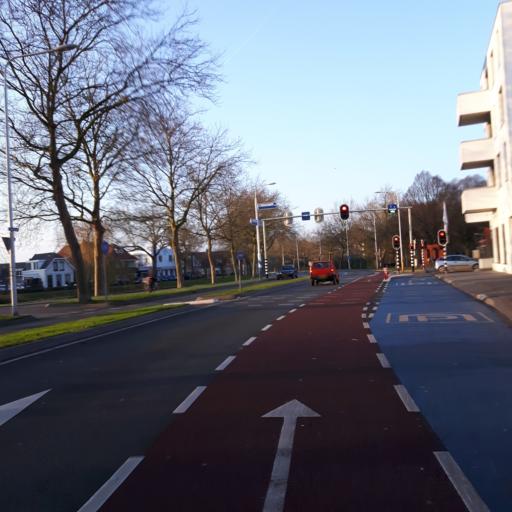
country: NL
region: Zeeland
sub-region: Gemeente Goes
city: Goes
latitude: 51.5029
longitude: 3.8873
